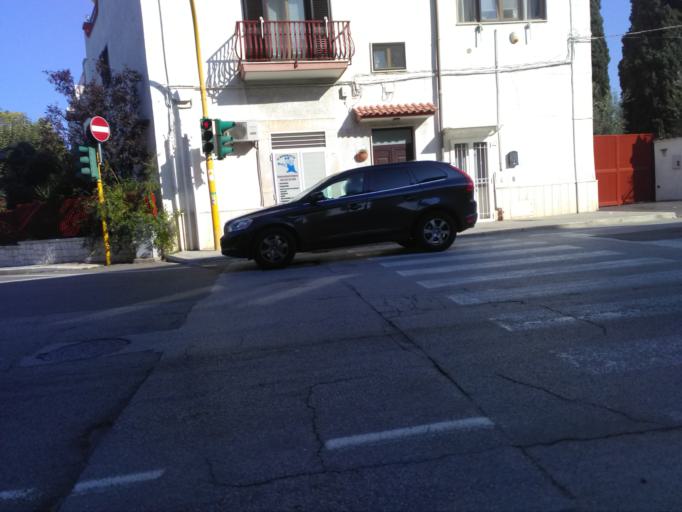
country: IT
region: Apulia
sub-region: Provincia di Bari
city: San Paolo
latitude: 41.1562
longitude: 16.7676
